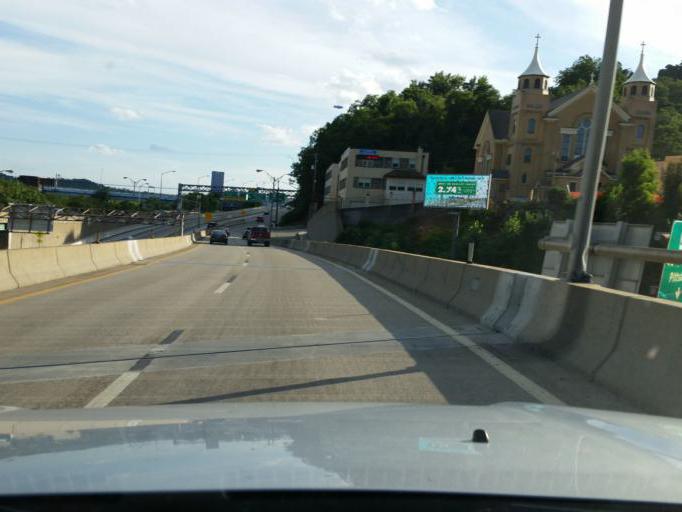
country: US
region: Pennsylvania
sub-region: Allegheny County
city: Millvale
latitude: 40.4777
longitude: -79.9687
